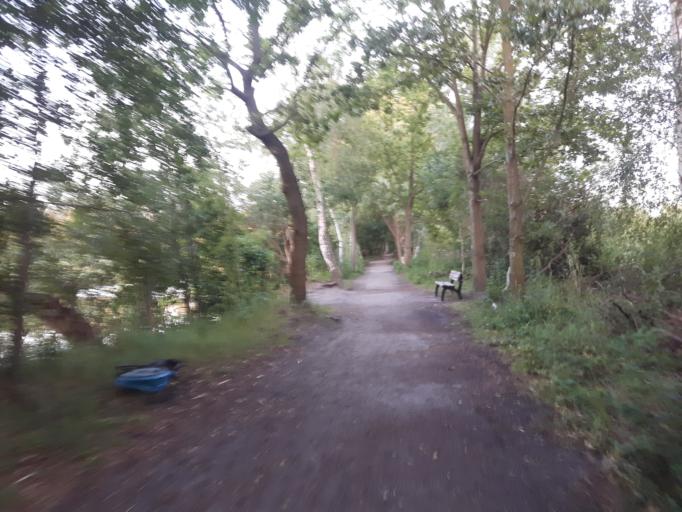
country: DE
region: Brandenburg
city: Falkensee
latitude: 52.5689
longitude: 13.1273
